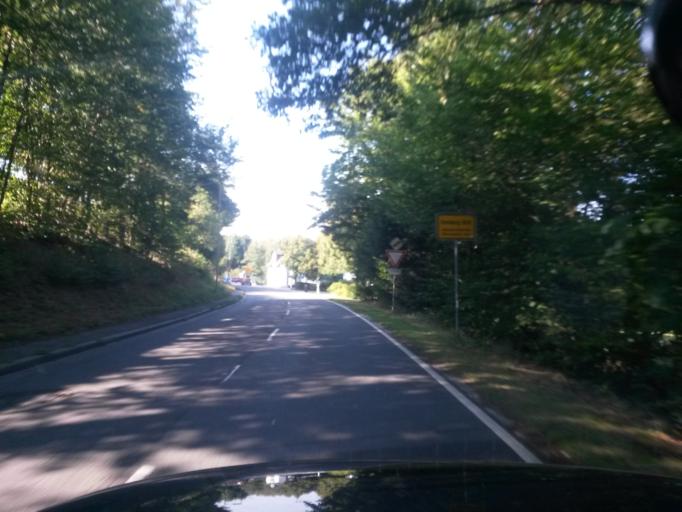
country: DE
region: North Rhine-Westphalia
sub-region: Regierungsbezirk Koln
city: Numbrecht
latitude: 50.9105
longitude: 7.5249
